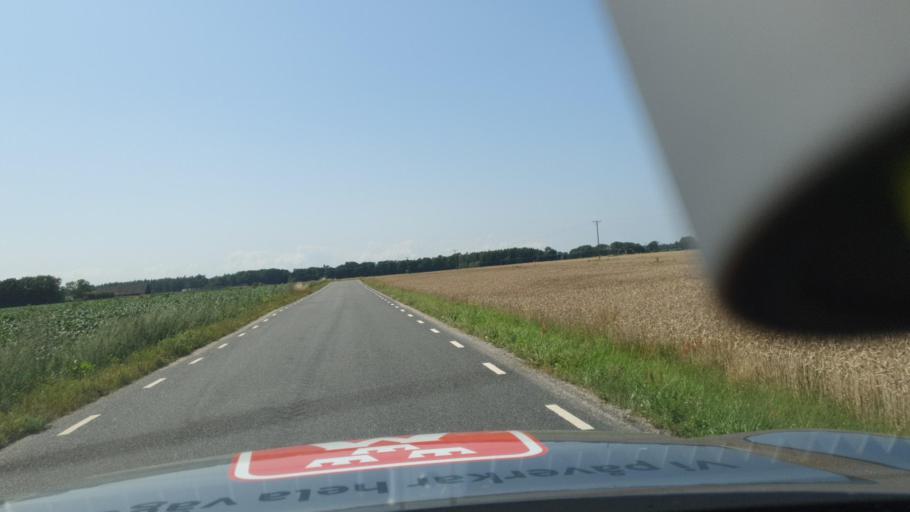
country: SE
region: Skane
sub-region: Bromolla Kommun
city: Bromoella
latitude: 56.0471
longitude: 14.4013
